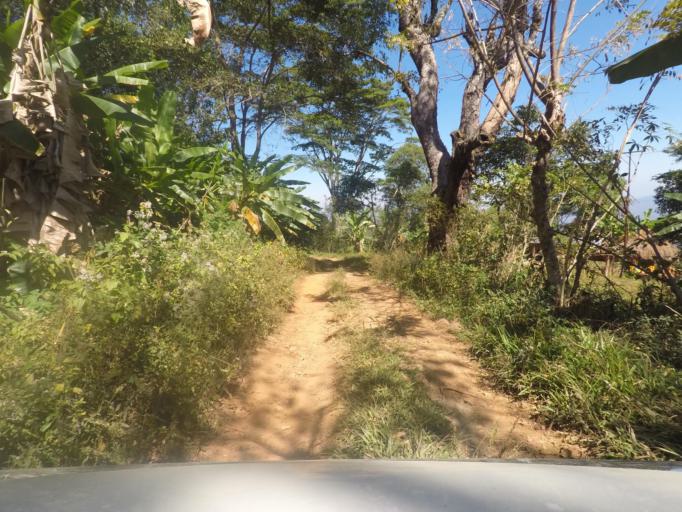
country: TL
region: Ermera
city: Gleno
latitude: -8.7187
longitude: 125.3199
